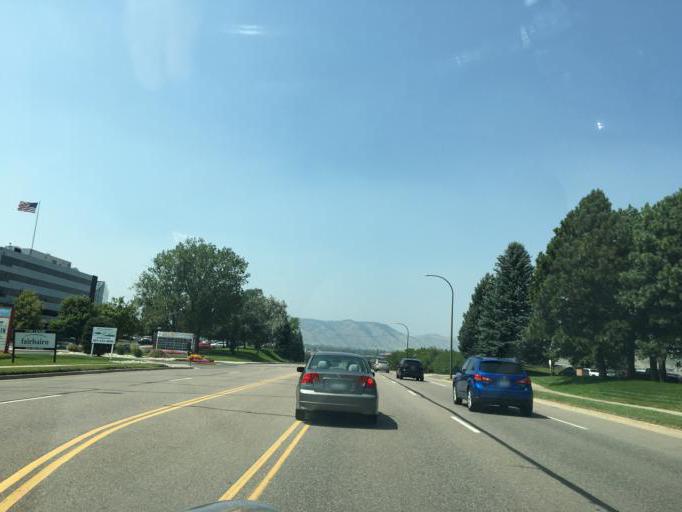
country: US
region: Colorado
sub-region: Jefferson County
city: Applewood
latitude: 39.7400
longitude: -105.1387
